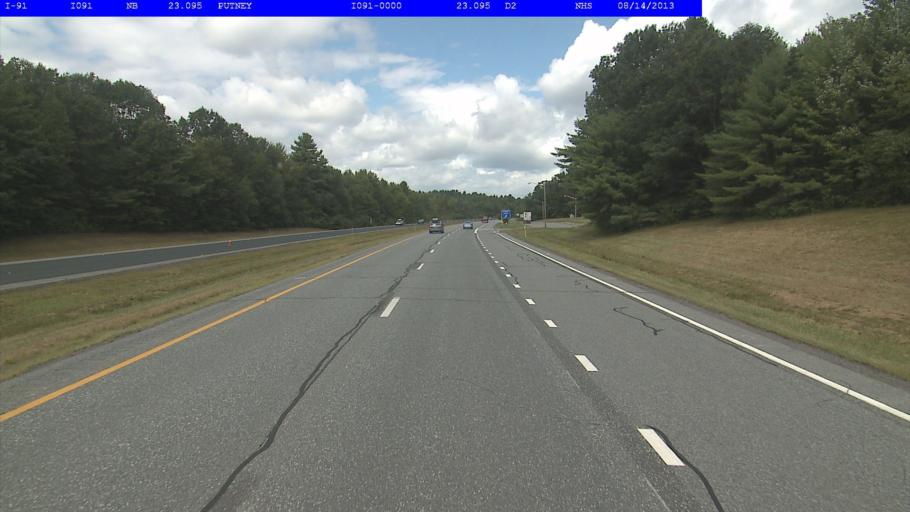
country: US
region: New Hampshire
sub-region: Cheshire County
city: Westmoreland
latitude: 43.0139
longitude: -72.4720
